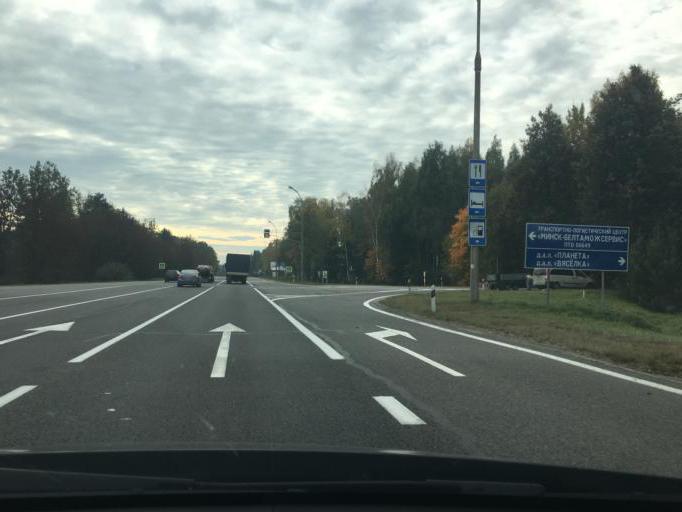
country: BY
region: Minsk
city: Azyartso
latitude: 53.7999
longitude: 27.3748
